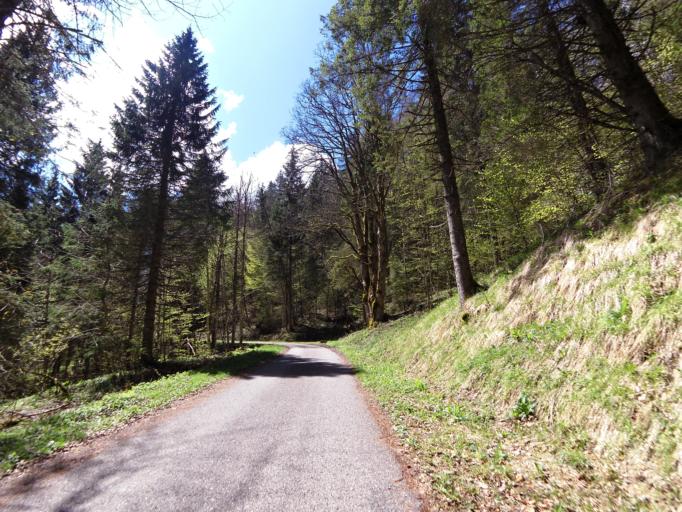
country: CH
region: Vaud
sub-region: Jura-Nord vaudois District
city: L'Abbaye
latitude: 46.6738
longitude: 6.3375
